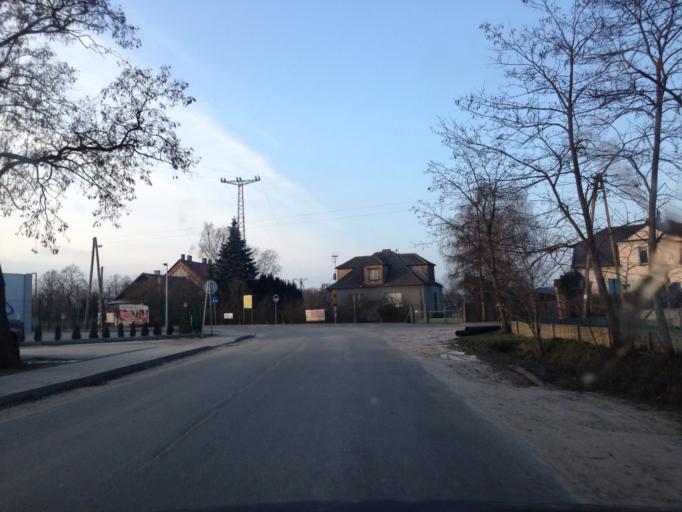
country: PL
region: Greater Poland Voivodeship
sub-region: Powiat poznanski
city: Kostrzyn
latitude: 52.4678
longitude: 17.1710
